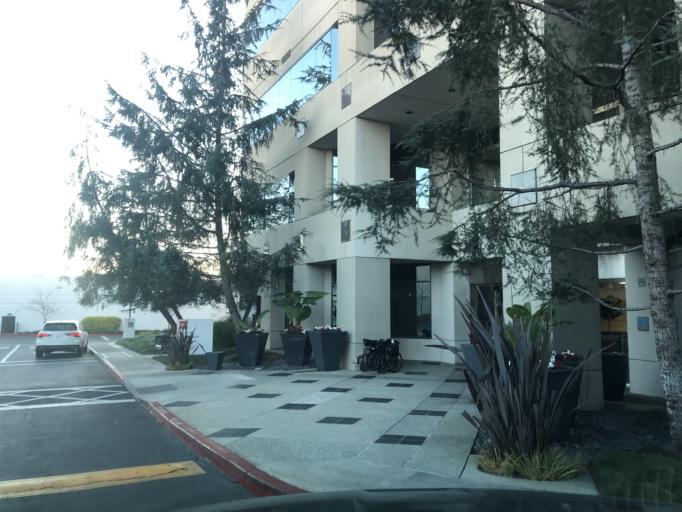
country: US
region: California
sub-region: Los Angeles County
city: Ladera Heights
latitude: 33.9887
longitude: -118.3661
